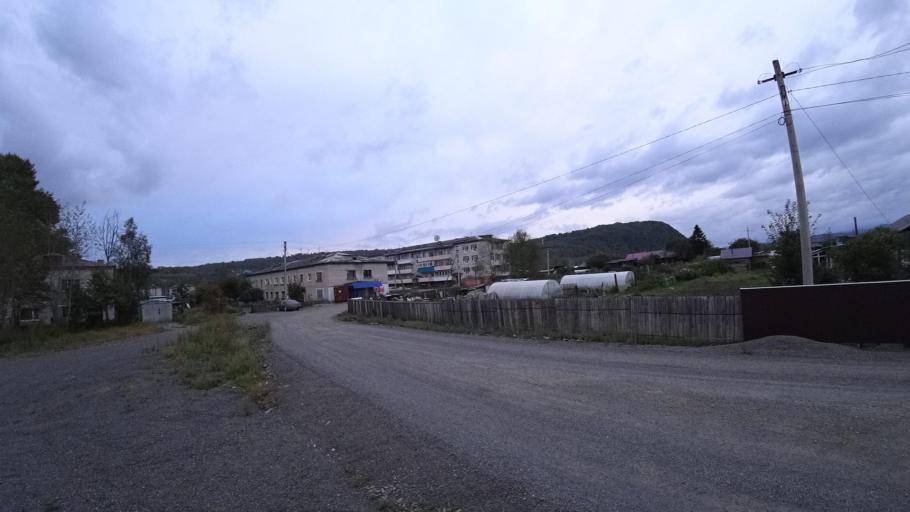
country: RU
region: Jewish Autonomous Oblast
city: Izvestkovyy
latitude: 48.9880
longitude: 131.5526
